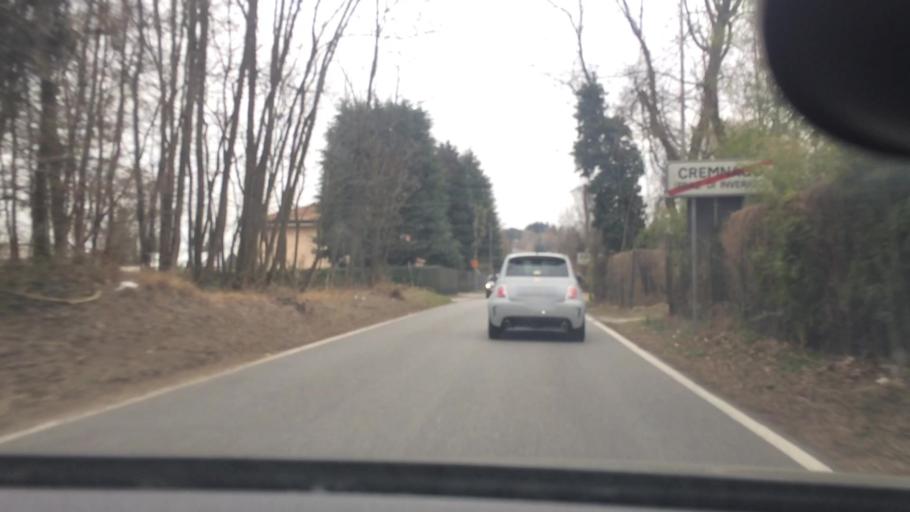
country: IT
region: Lombardy
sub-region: Provincia di Como
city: Arosio
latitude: 45.7304
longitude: 9.2060
